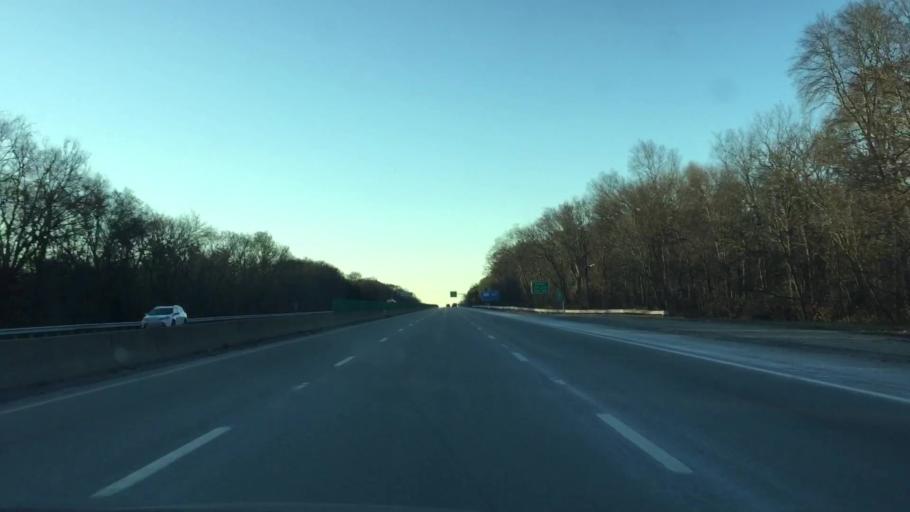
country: US
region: Massachusetts
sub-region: Norfolk County
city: Avon
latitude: 42.1168
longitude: -71.0606
